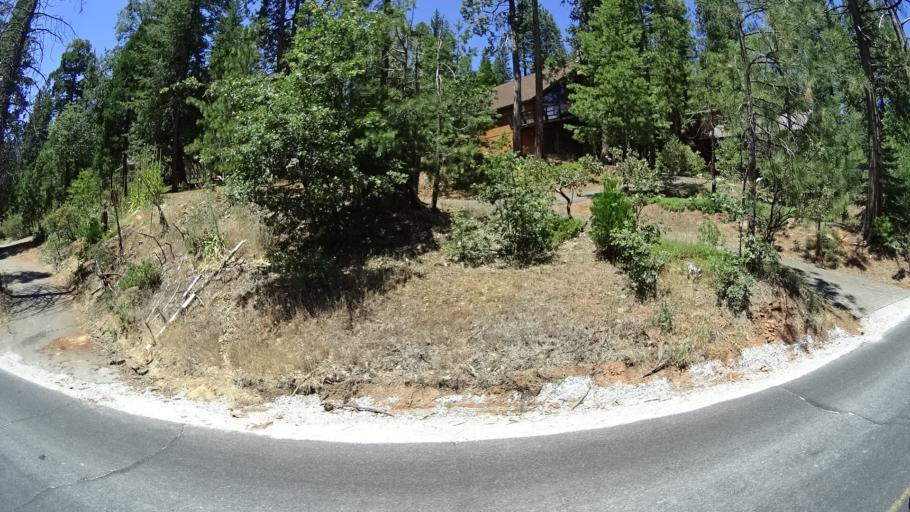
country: US
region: California
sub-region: Calaveras County
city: Arnold
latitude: 38.2455
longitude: -120.3366
